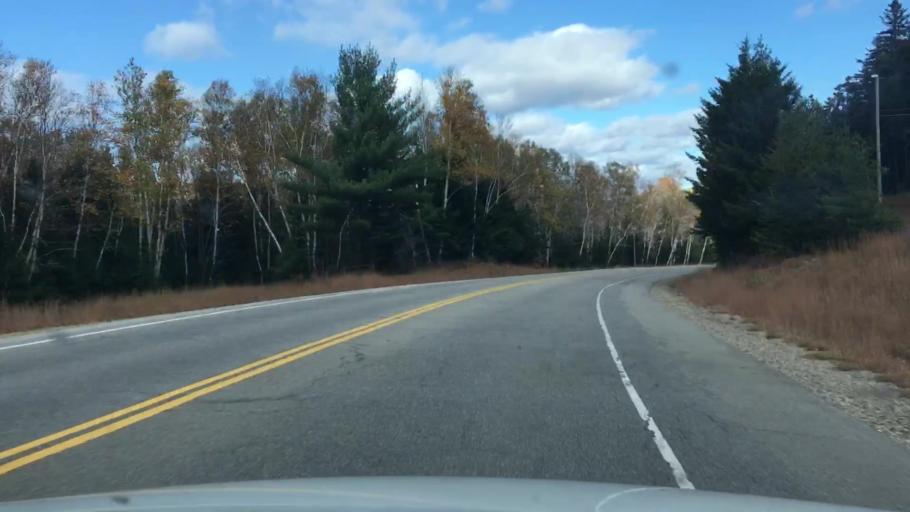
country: US
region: New Hampshire
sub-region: Coos County
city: Gorham
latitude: 44.2988
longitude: -71.2243
